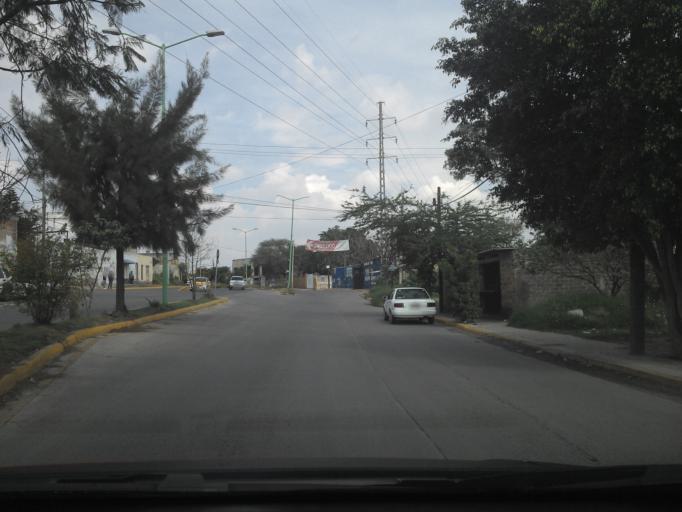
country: MX
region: Jalisco
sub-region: Tlajomulco de Zuniga
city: Altus Bosques
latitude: 20.5894
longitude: -103.3505
